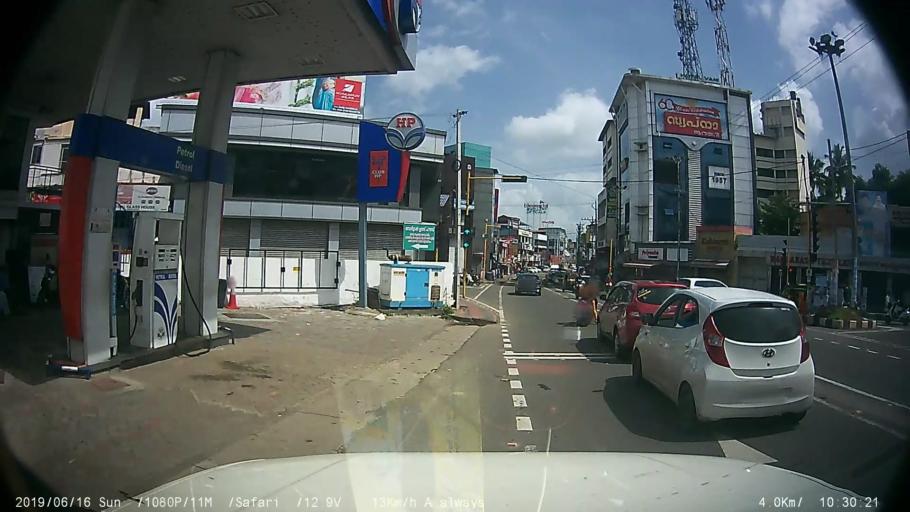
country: IN
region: Kerala
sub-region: Kottayam
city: Changanacheri
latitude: 9.4462
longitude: 76.5406
